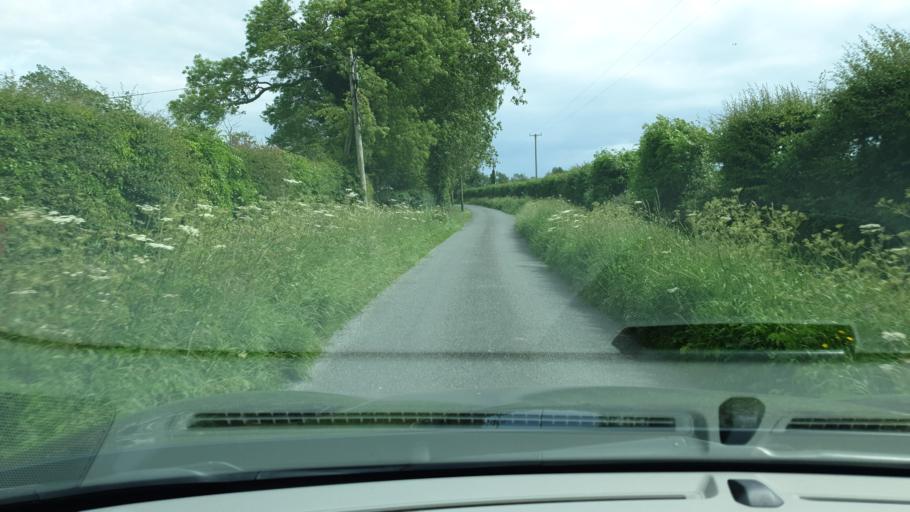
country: IE
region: Leinster
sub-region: An Mhi
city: Ratoath
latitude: 53.4593
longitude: -6.4614
